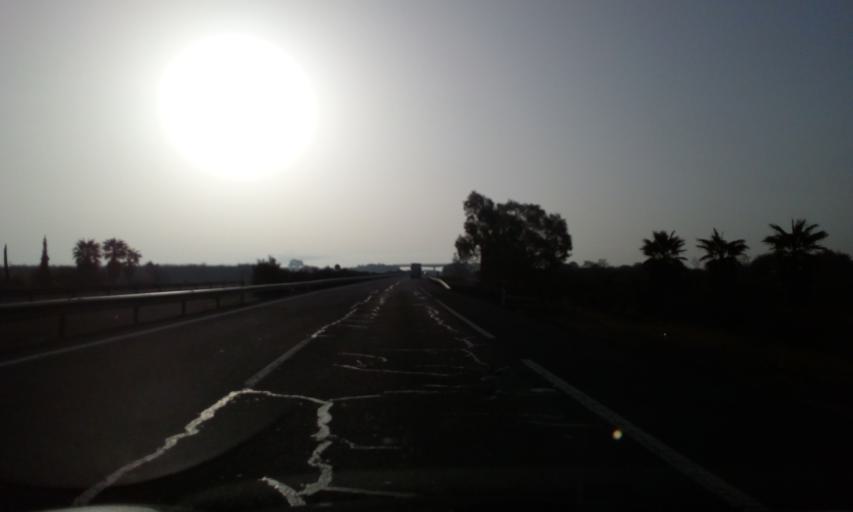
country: ES
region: Andalusia
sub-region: Provincia de Huelva
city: Gibraleon
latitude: 37.3465
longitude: -6.9251
